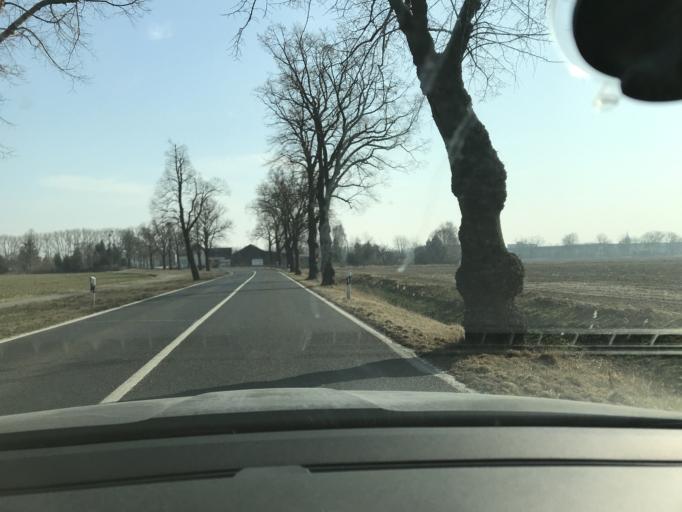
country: DE
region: Brandenburg
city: Mittenwalde
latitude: 52.2779
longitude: 13.5323
